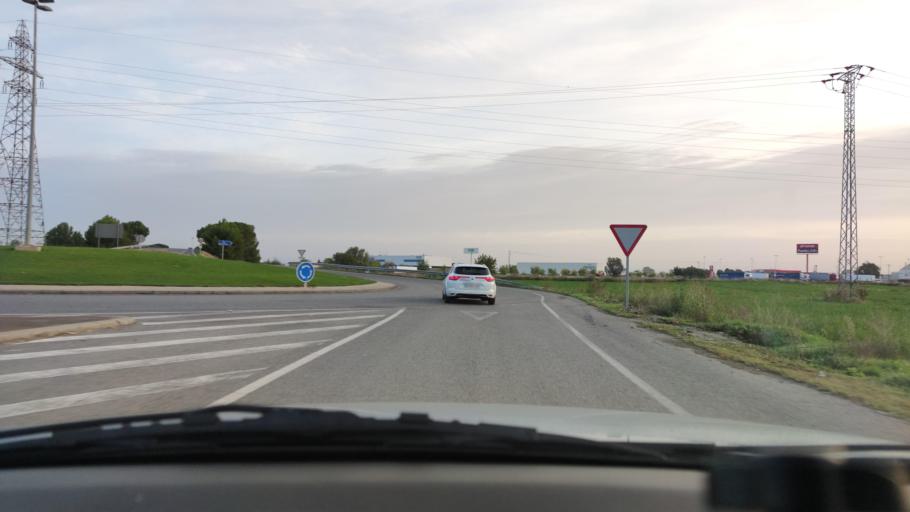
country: ES
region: Catalonia
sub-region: Provincia de Lleida
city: Mollerussa
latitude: 41.6377
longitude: 0.8751
